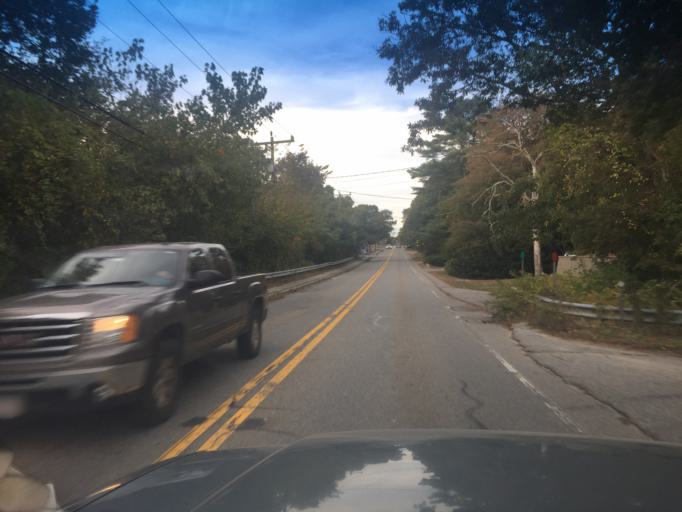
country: US
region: Massachusetts
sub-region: Barnstable County
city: North Falmouth
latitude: 41.6491
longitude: -70.6121
